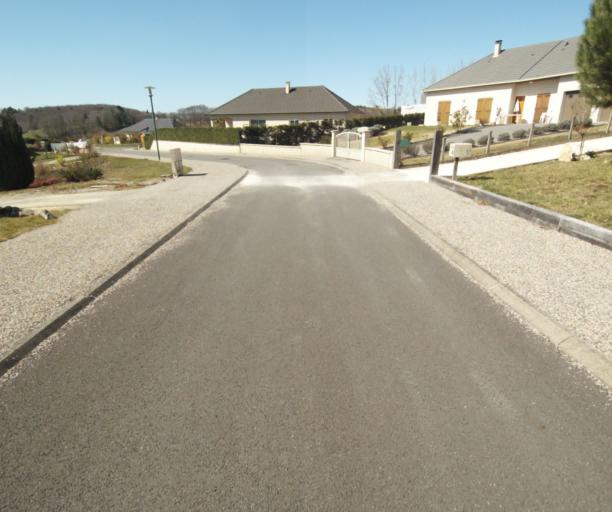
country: FR
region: Limousin
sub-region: Departement de la Correze
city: Saint-Mexant
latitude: 45.2779
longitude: 1.6555
